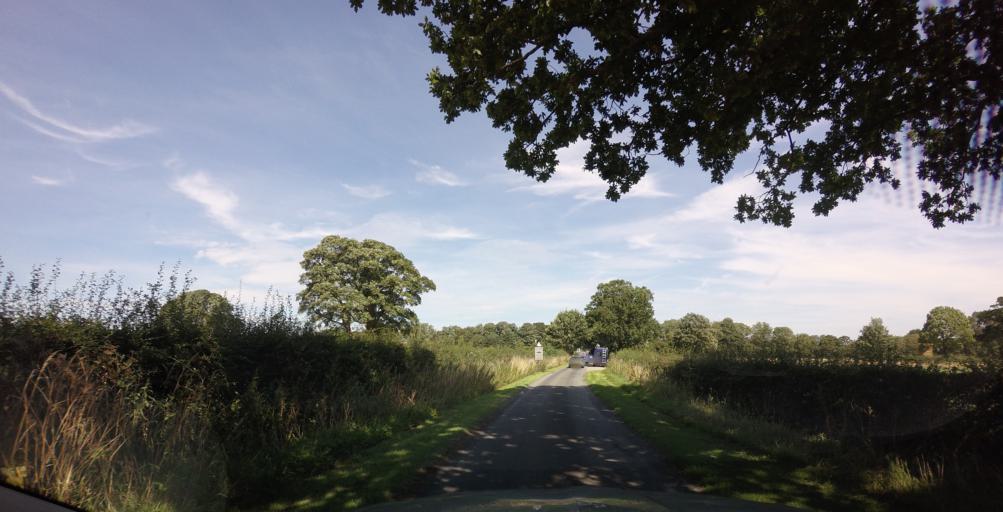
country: GB
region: England
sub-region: North Yorkshire
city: Ripon
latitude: 54.1218
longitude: -1.4849
